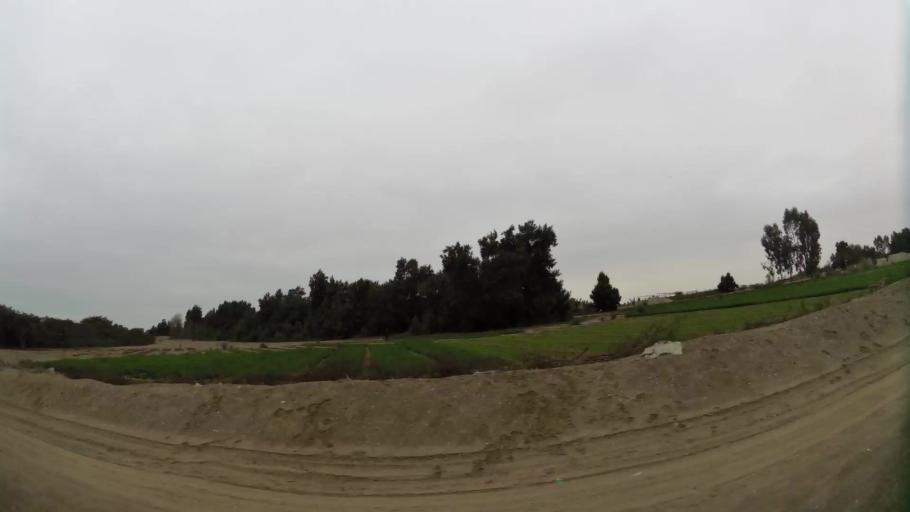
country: PE
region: Ica
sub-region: Provincia de Pisco
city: Pisco
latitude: -13.7478
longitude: -76.1918
